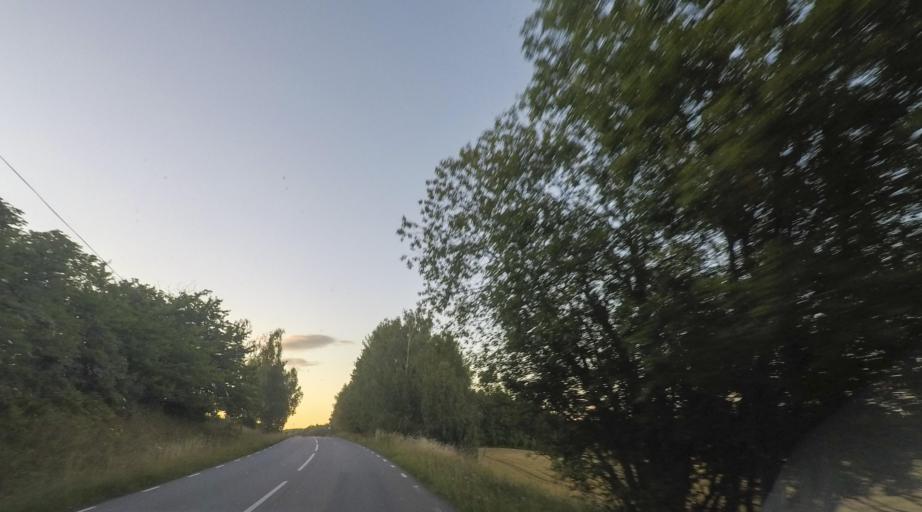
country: SE
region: Soedermanland
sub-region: Trosa Kommun
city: Trosa
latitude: 58.9754
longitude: 17.6931
